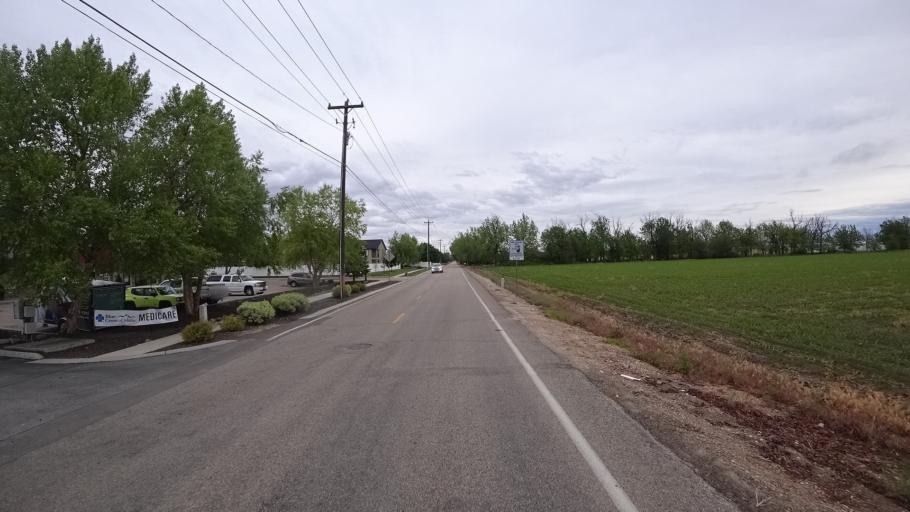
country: US
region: Idaho
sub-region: Ada County
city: Star
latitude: 43.6924
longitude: -116.4733
